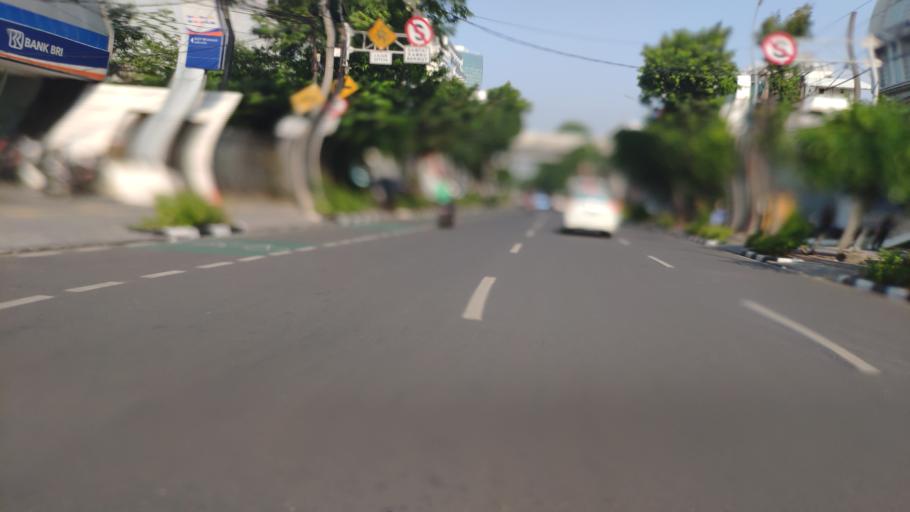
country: ID
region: Jakarta Raya
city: Jakarta
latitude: -6.2458
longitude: 106.7965
